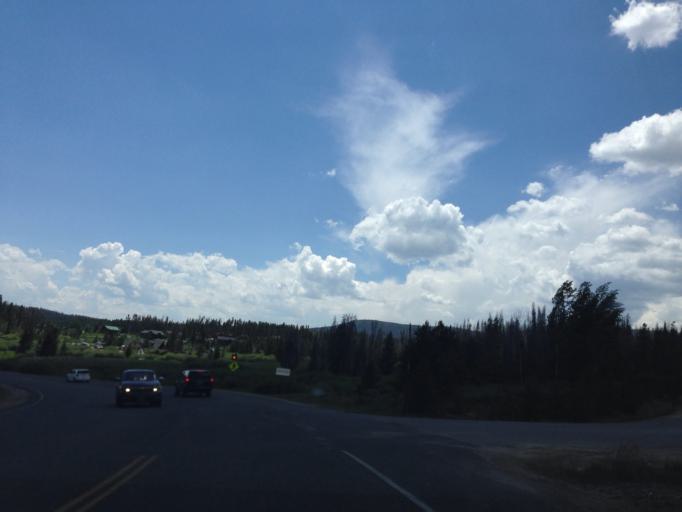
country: US
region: Colorado
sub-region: Grand County
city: Granby
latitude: 40.2586
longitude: -105.8375
